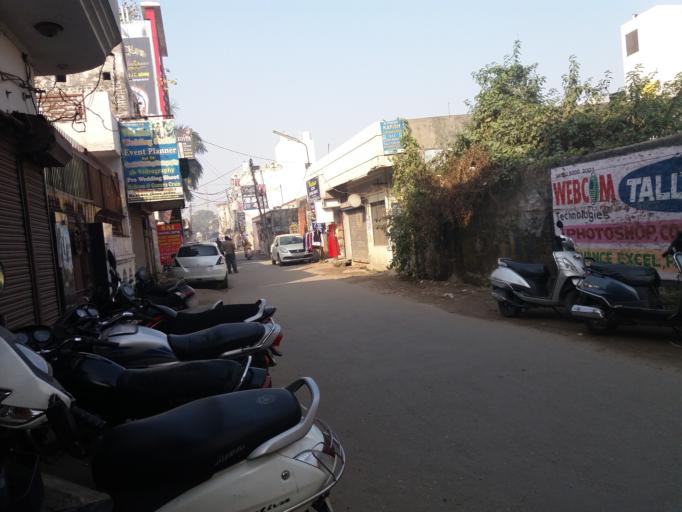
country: IN
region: Haryana
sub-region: Yamunanagar
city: Yamunanagar
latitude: 30.1315
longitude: 77.2928
